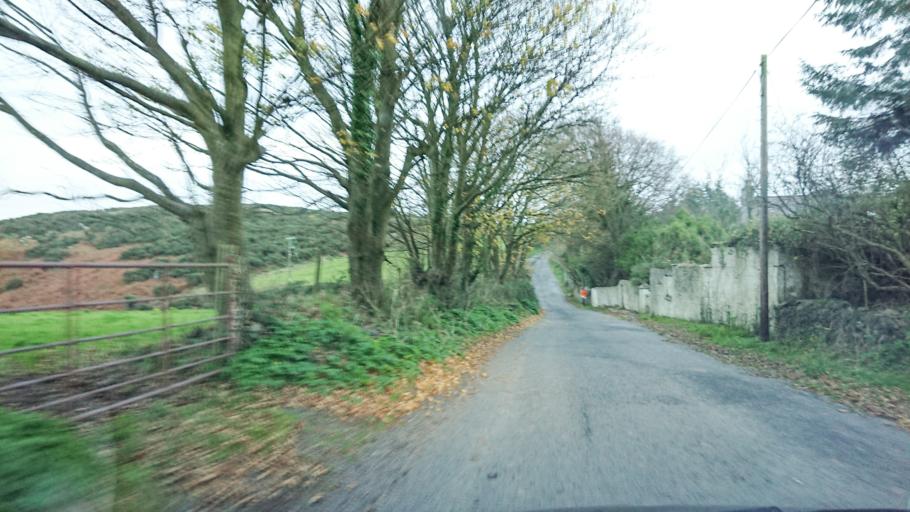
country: IE
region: Munster
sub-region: Waterford
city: Dunmore East
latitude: 52.2383
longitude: -6.9764
